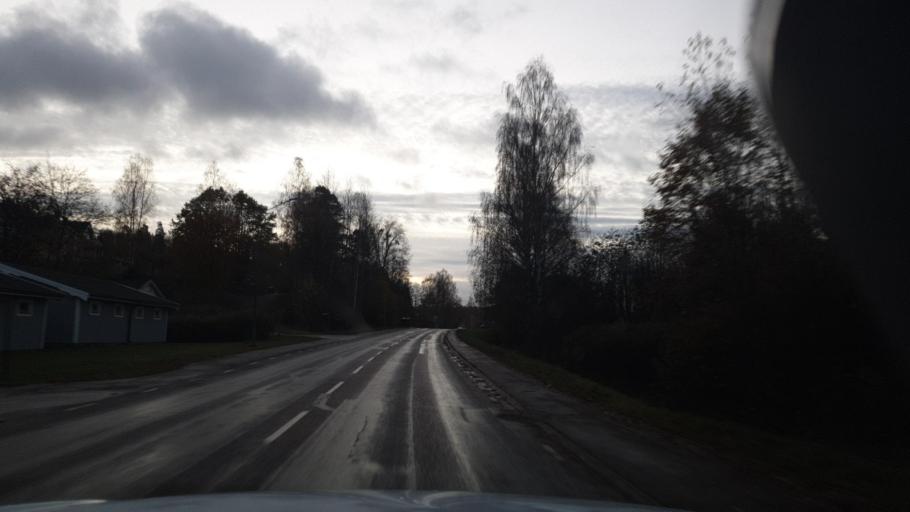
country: SE
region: Vaermland
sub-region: Arvika Kommun
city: Arvika
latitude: 59.6281
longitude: 12.8270
